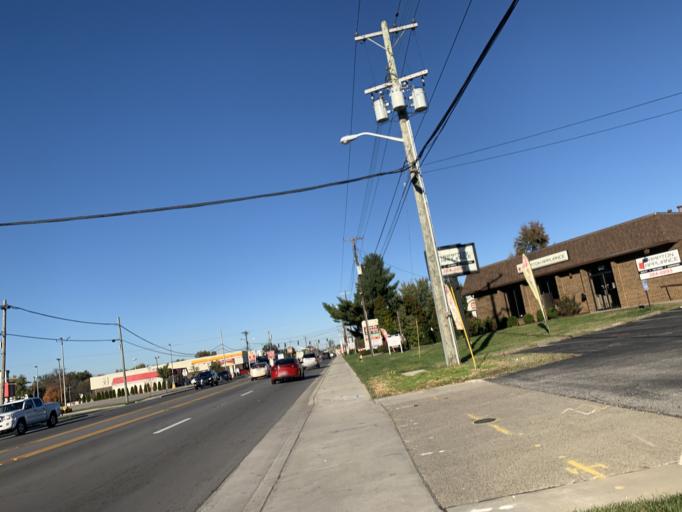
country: US
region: Kentucky
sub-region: Jefferson County
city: Shively
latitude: 38.1880
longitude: -85.8109
